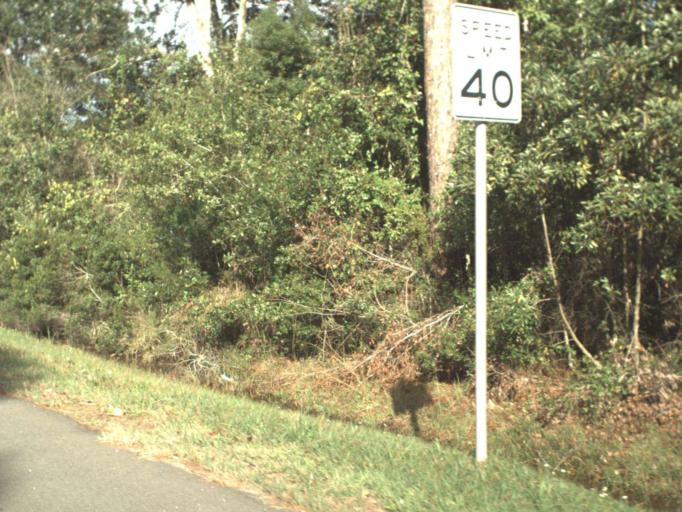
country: US
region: Florida
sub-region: Escambia County
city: Warrington
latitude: 30.3823
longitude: -87.3083
